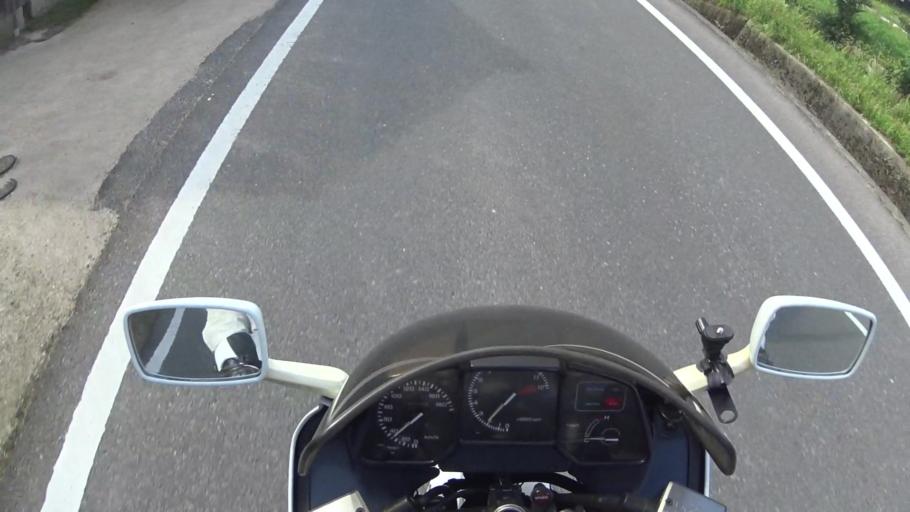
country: JP
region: Kyoto
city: Miyazu
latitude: 35.6541
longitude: 135.0974
